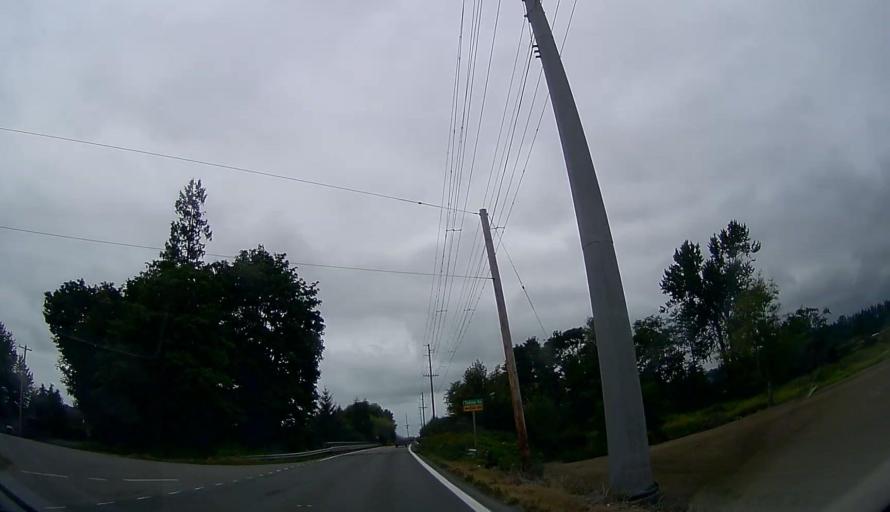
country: US
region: Washington
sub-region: Snohomish County
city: Stanwood
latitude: 48.2252
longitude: -122.3375
